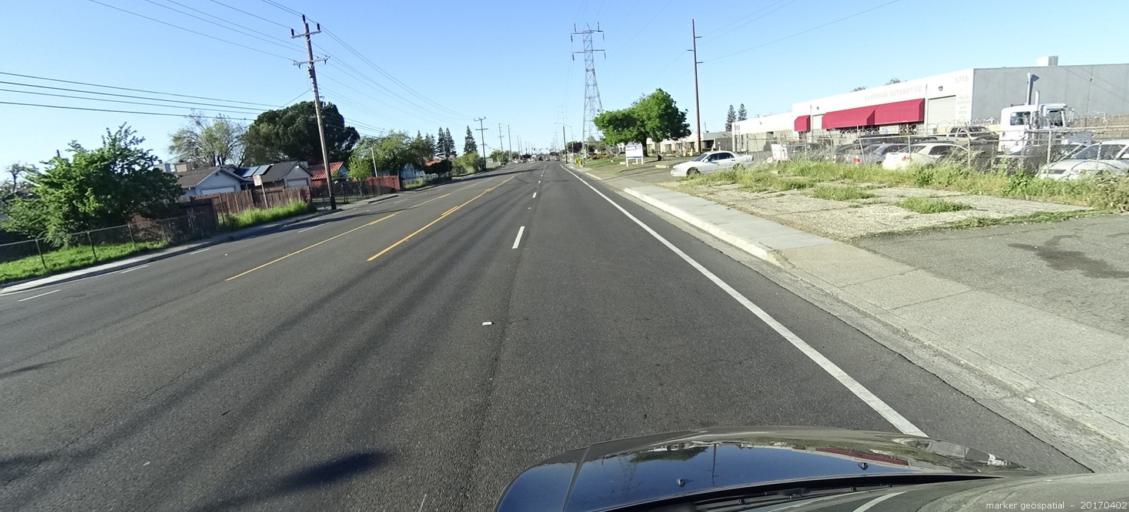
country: US
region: California
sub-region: Sacramento County
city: Florin
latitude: 38.5220
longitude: -121.4091
